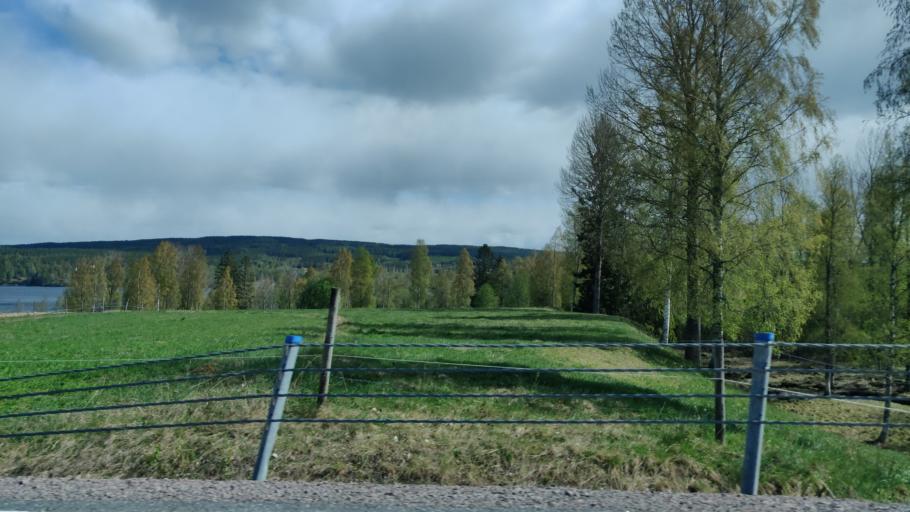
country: SE
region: Vaermland
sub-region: Munkfors Kommun
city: Munkfors
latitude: 59.8558
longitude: 13.7064
